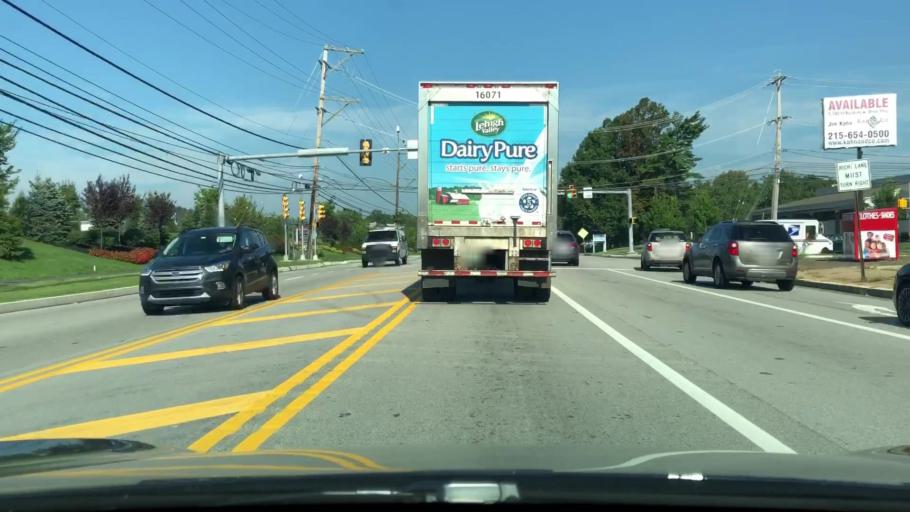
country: US
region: Pennsylvania
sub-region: Montgomery County
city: Dresher
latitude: 40.1614
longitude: -75.1506
